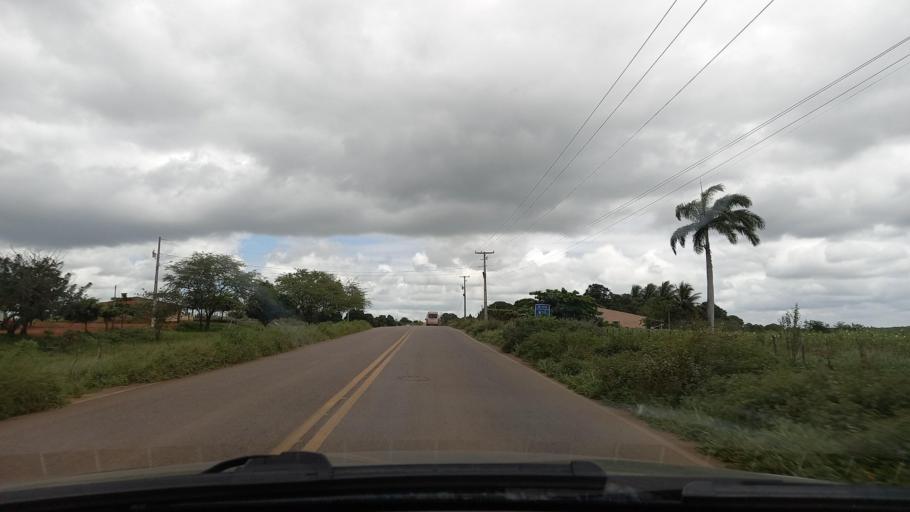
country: BR
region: Sergipe
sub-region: Caninde De Sao Francisco
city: Caninde de Sao Francisco
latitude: -9.6797
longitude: -37.8064
